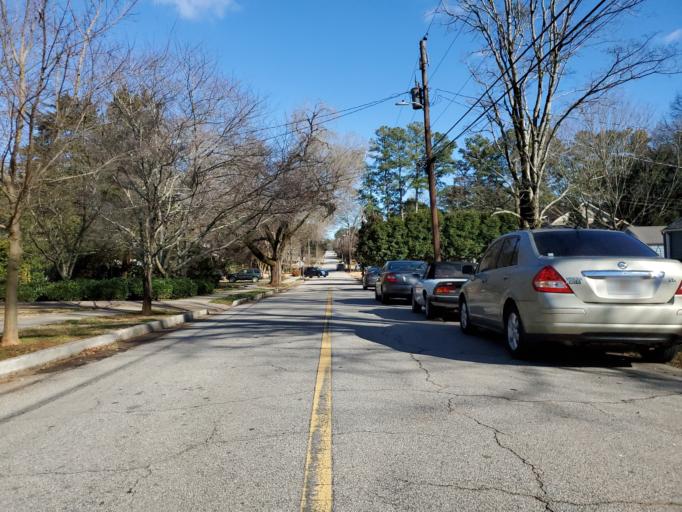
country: US
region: Georgia
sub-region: DeKalb County
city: Avondale Estates
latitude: 33.7717
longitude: -84.2596
